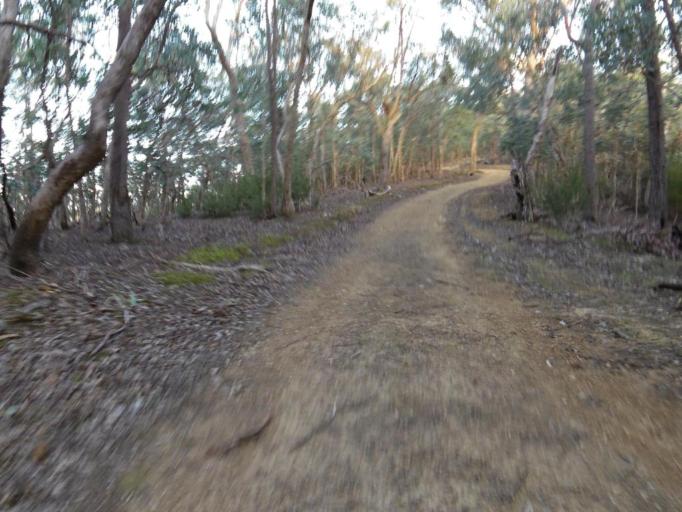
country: AU
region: Victoria
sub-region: Nillumbik
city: North Warrandyte
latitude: -37.7238
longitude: 145.2384
